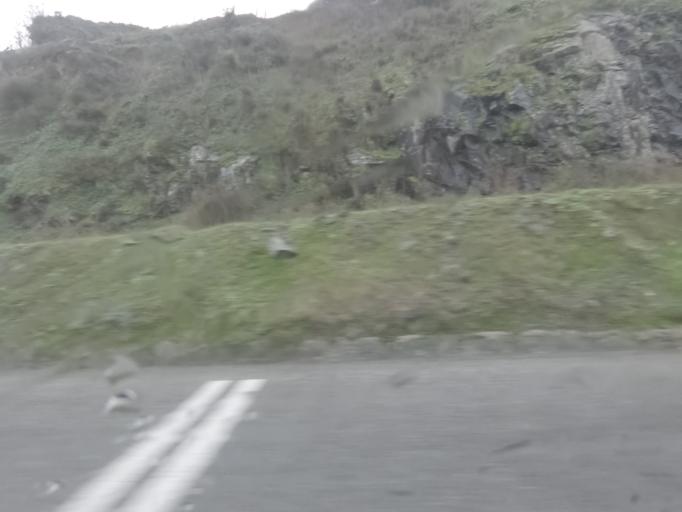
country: PT
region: Vila Real
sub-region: Peso da Regua
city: Peso da Regua
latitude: 41.1684
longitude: -7.7659
